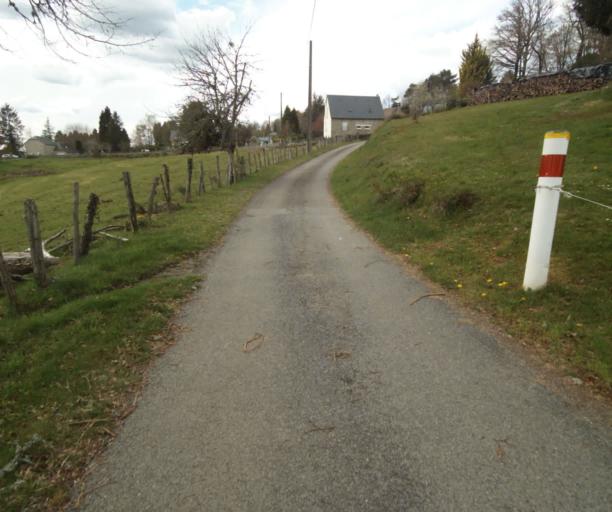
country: FR
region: Limousin
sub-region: Departement de la Correze
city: Argentat
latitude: 45.1890
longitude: 1.9576
